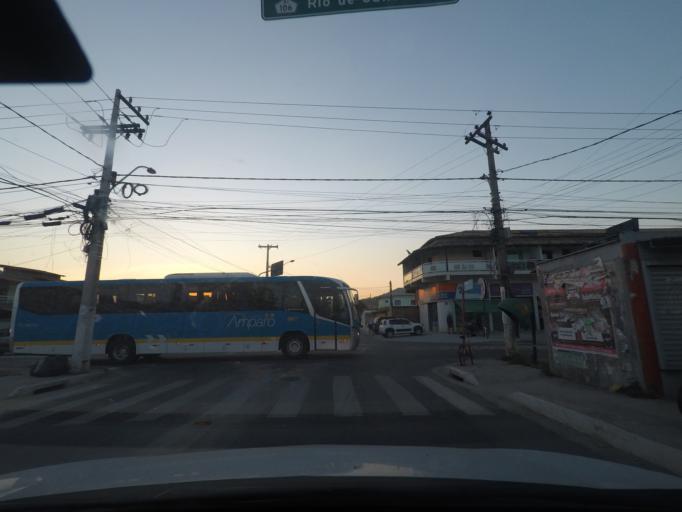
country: BR
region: Rio de Janeiro
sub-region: Marica
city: Marica
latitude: -22.9567
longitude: -42.9620
